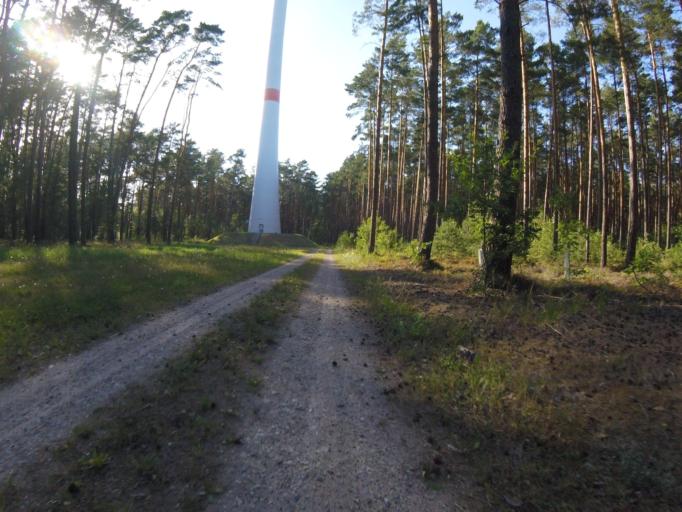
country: DE
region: Berlin
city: Schmockwitz
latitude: 52.3375
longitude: 13.7248
